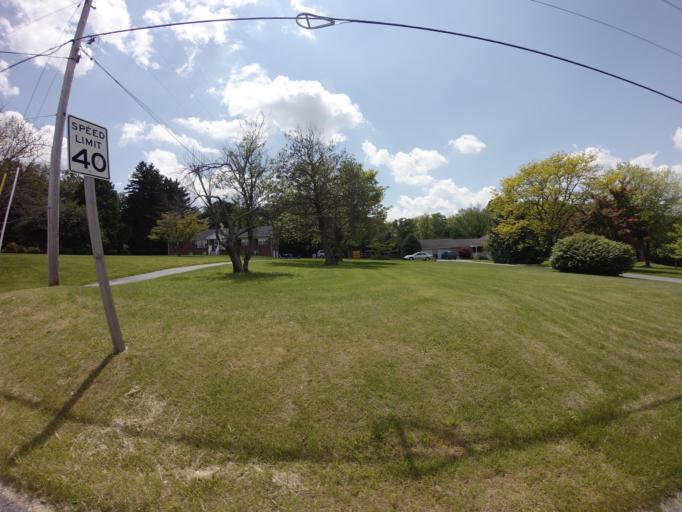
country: US
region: Maryland
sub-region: Montgomery County
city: Damascus
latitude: 39.3335
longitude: -77.2240
